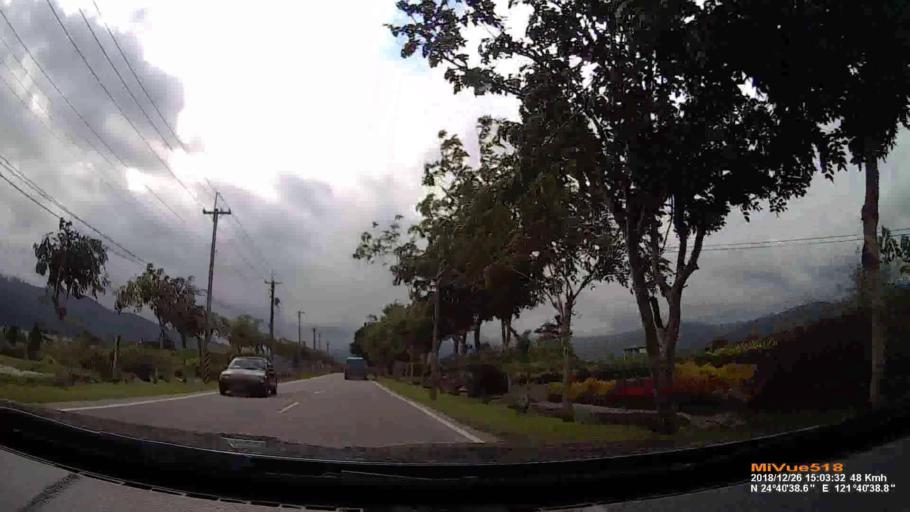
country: TW
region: Taiwan
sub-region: Yilan
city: Yilan
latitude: 24.6680
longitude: 121.6502
